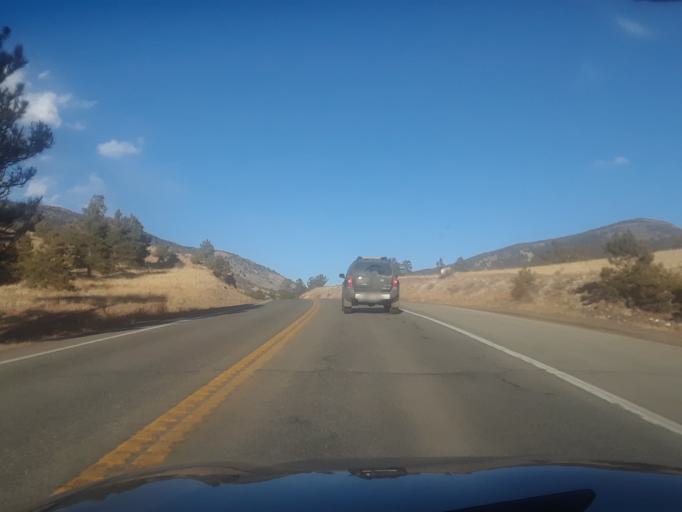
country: US
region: Colorado
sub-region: Chaffee County
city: Buena Vista
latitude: 38.8419
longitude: -105.9955
